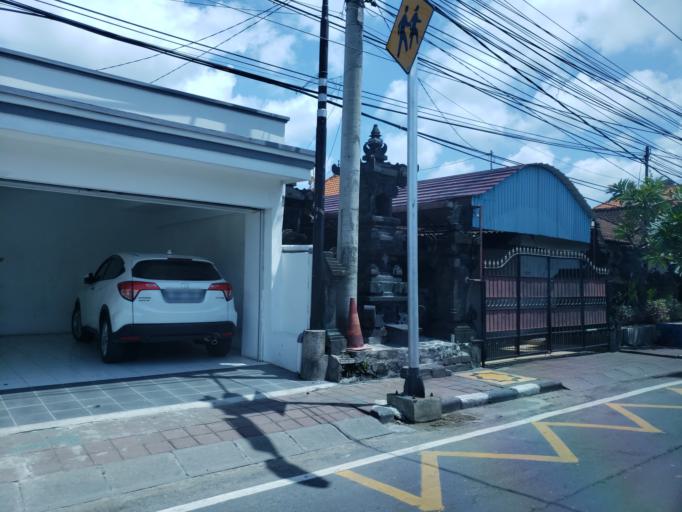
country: ID
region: Bali
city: Kelanabian
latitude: -8.7680
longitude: 115.1739
